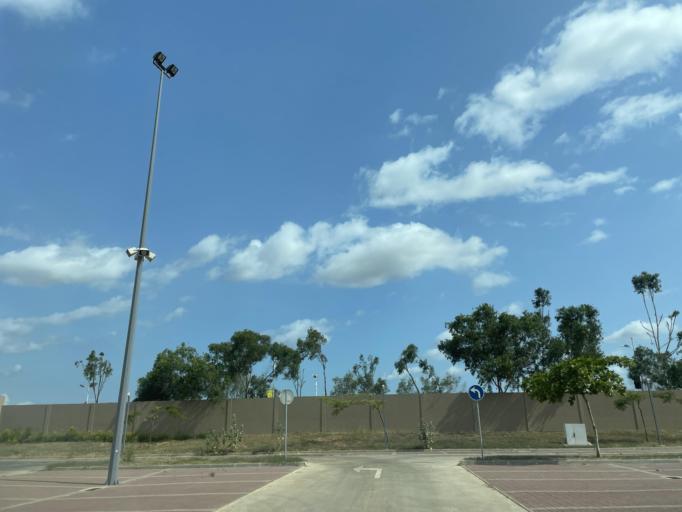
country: AO
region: Luanda
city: Luanda
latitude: -8.9907
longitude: 13.2872
